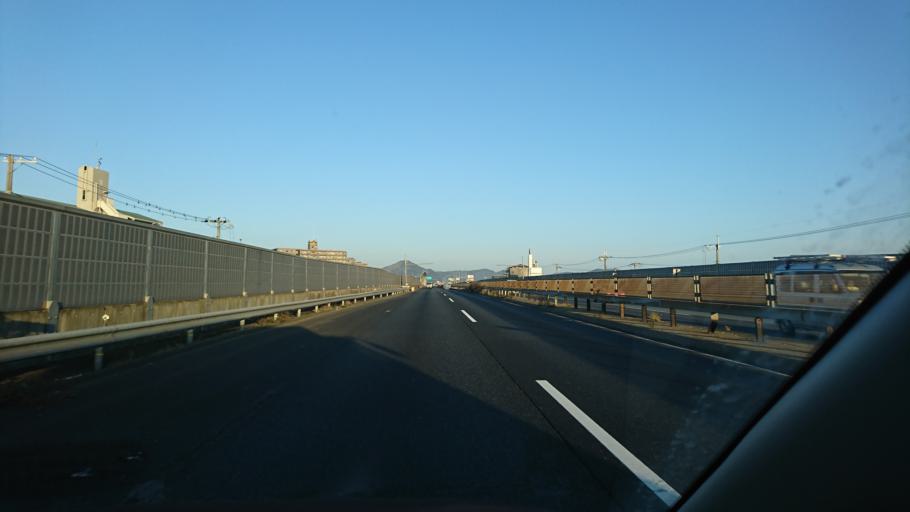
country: JP
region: Hyogo
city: Kakogawacho-honmachi
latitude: 34.7711
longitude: 134.8441
